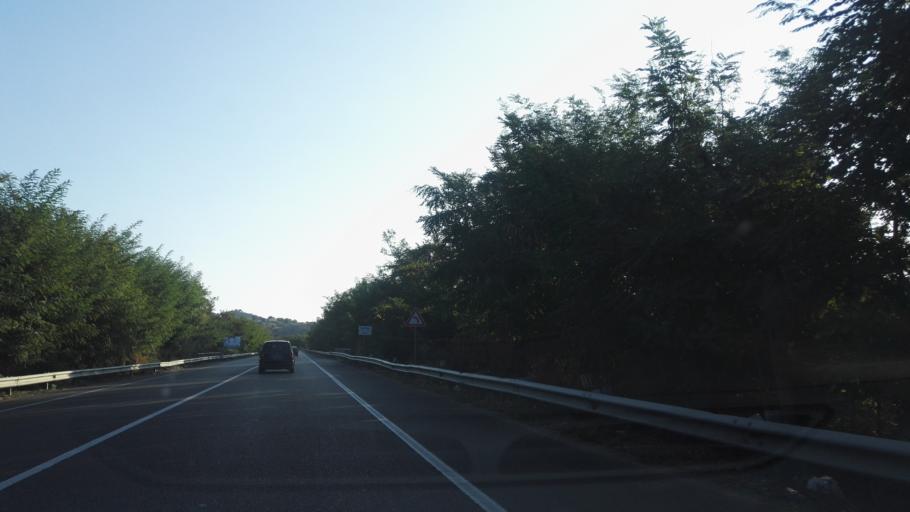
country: IT
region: Calabria
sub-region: Provincia di Catanzaro
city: Montepaone Lido
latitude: 38.7344
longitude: 16.5430
